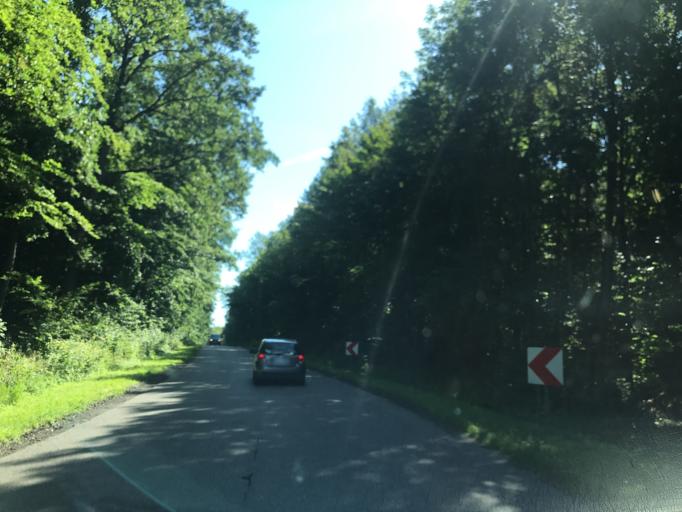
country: PL
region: Pomeranian Voivodeship
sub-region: Powiat slupski
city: Potegowo
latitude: 54.4081
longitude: 17.4248
